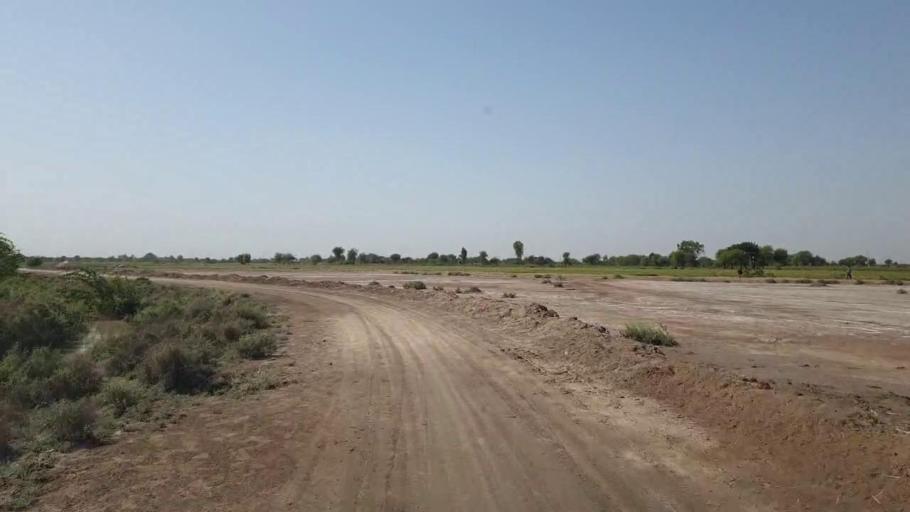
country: PK
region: Sindh
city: Tando Bago
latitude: 24.7395
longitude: 69.0227
